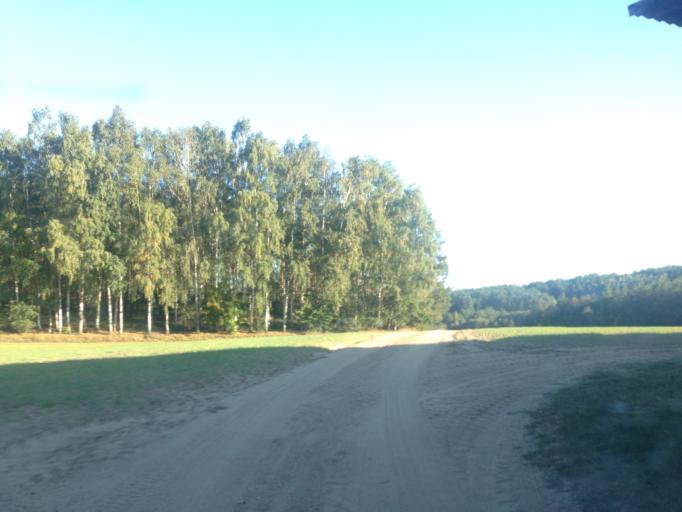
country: PL
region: Kujawsko-Pomorskie
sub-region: Powiat brodnicki
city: Bartniczka
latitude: 53.2773
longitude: 19.6060
